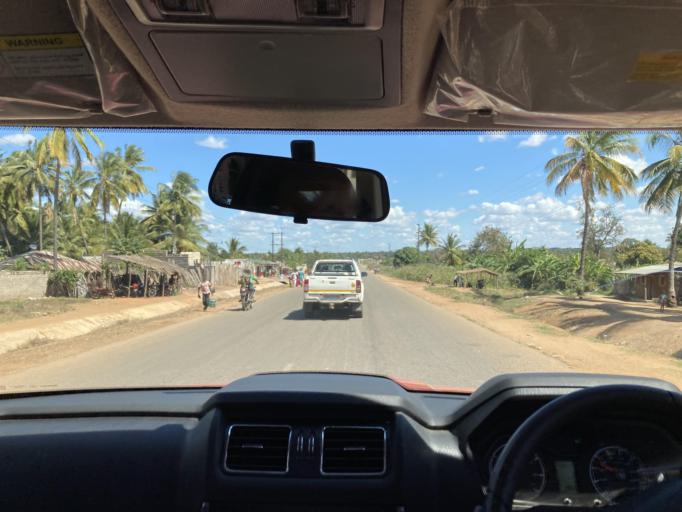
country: MZ
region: Cabo Delgado
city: Montepuez
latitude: -13.1338
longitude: 38.9917
